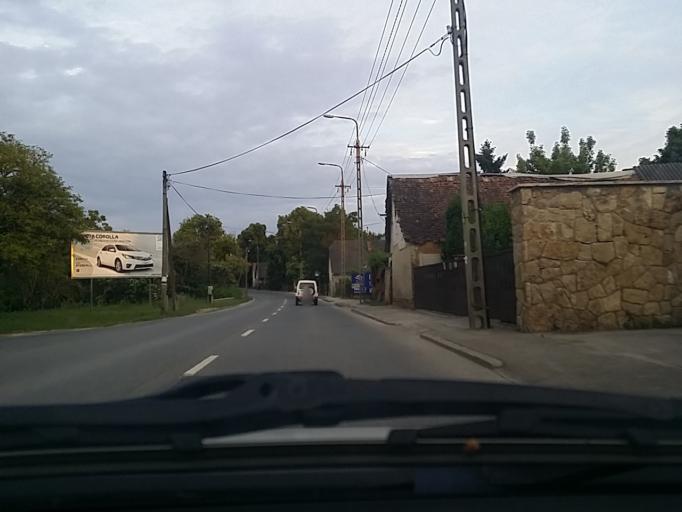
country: HU
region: Pest
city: Solymar
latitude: 47.5659
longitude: 18.9565
